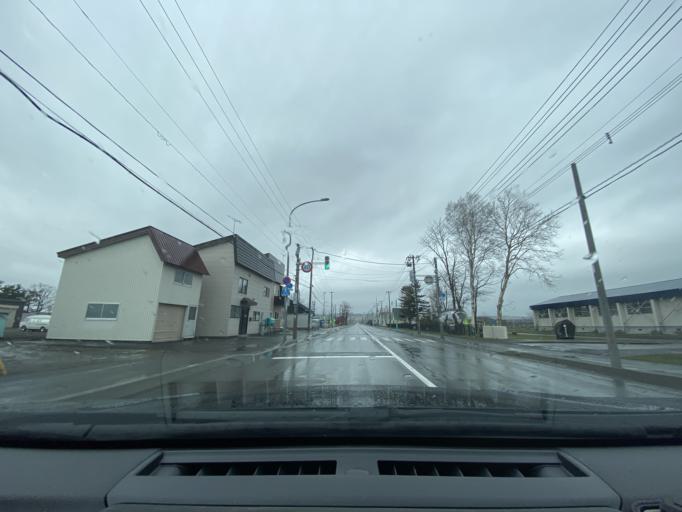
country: JP
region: Hokkaido
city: Fukagawa
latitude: 43.8078
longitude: 141.9249
